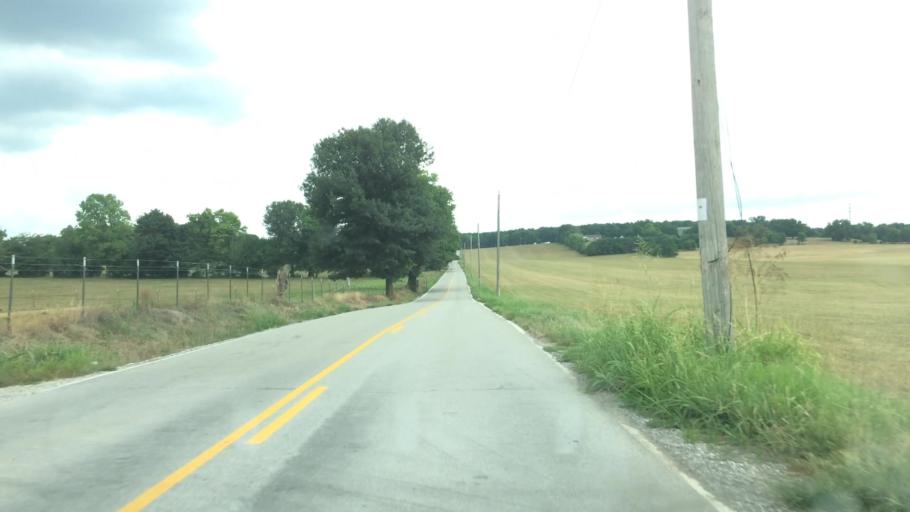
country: US
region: Missouri
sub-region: Greene County
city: Strafford
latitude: 37.1812
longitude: -93.1847
